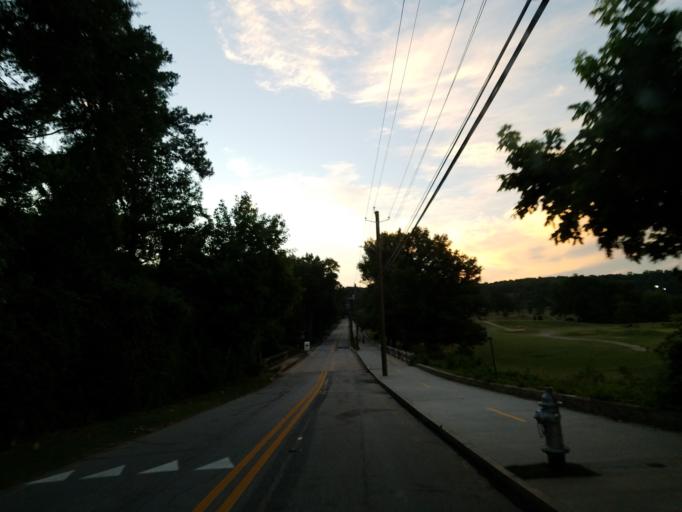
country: US
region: Georgia
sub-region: DeKalb County
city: North Atlanta
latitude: 33.8672
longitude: -84.3927
